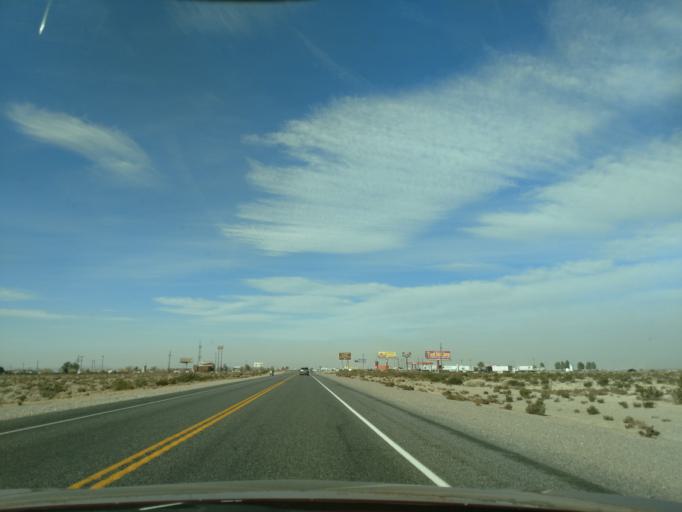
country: US
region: Nevada
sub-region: Nye County
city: Beatty
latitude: 36.6417
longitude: -116.3916
